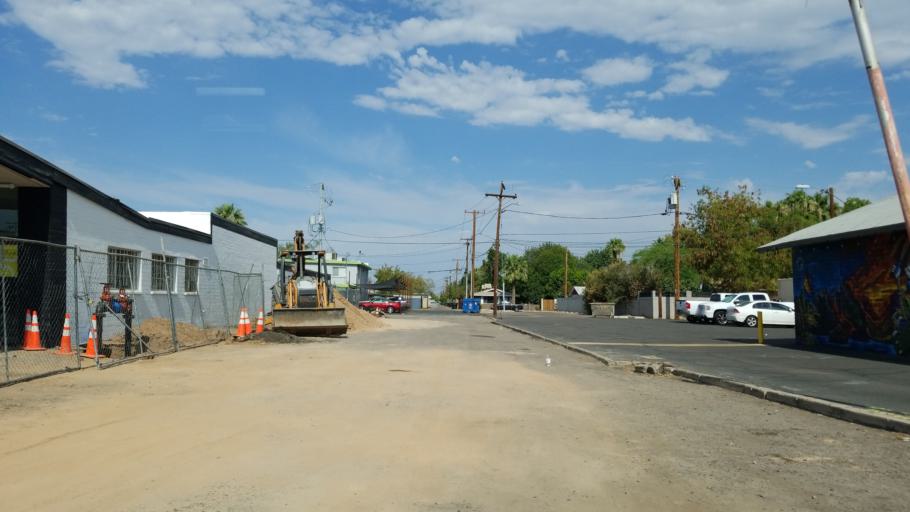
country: US
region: Arizona
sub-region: Maricopa County
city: Phoenix
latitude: 33.4962
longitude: -112.0836
